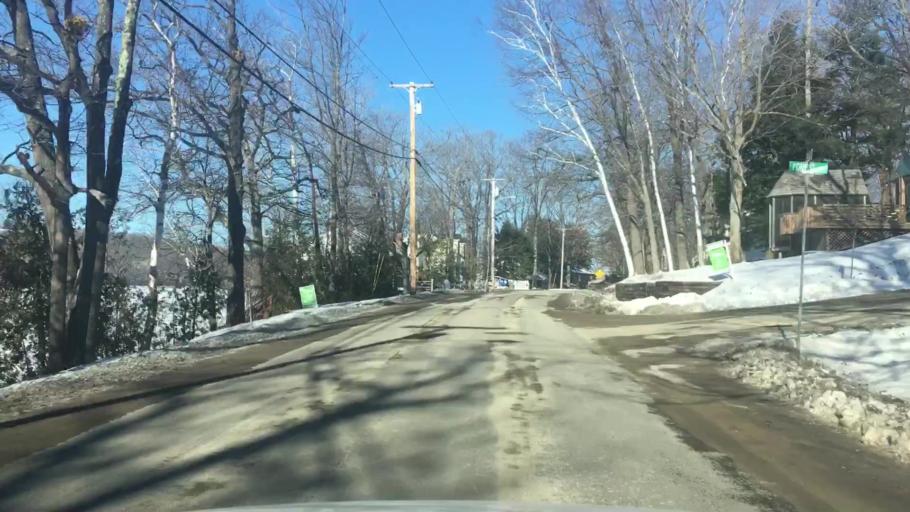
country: US
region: Maine
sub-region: Kennebec County
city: Winthrop
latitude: 44.3126
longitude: -69.9696
